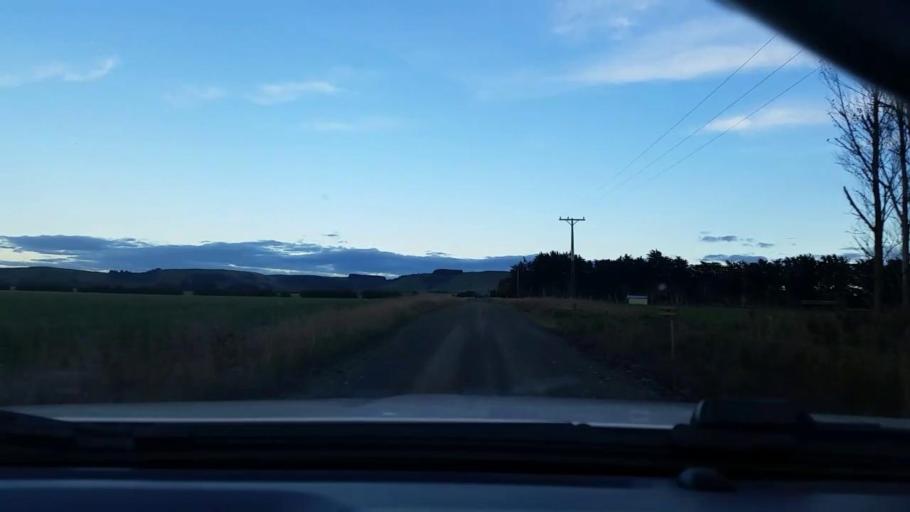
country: NZ
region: Southland
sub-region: Southland District
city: Winton
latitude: -46.1074
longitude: 168.4462
